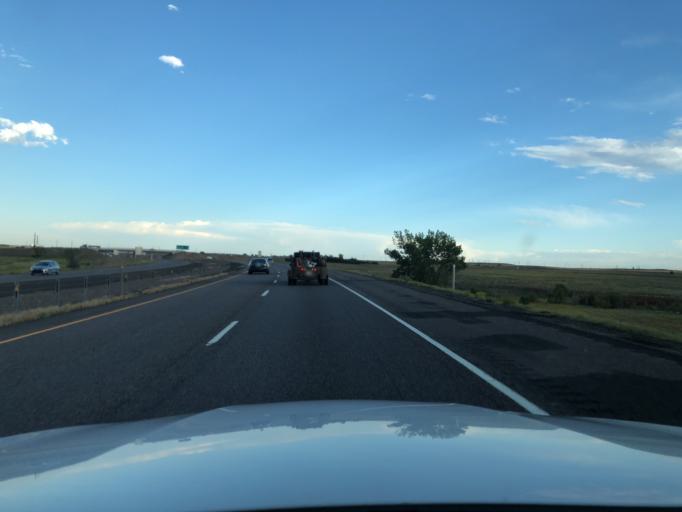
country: US
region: Colorado
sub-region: Adams County
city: Brighton
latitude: 39.9087
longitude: -104.7776
